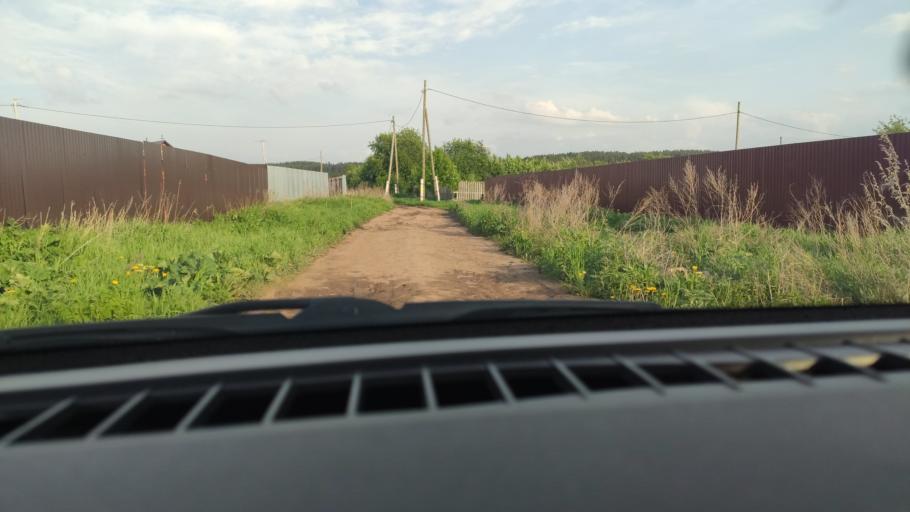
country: RU
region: Perm
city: Kultayevo
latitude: 57.8979
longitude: 55.9974
